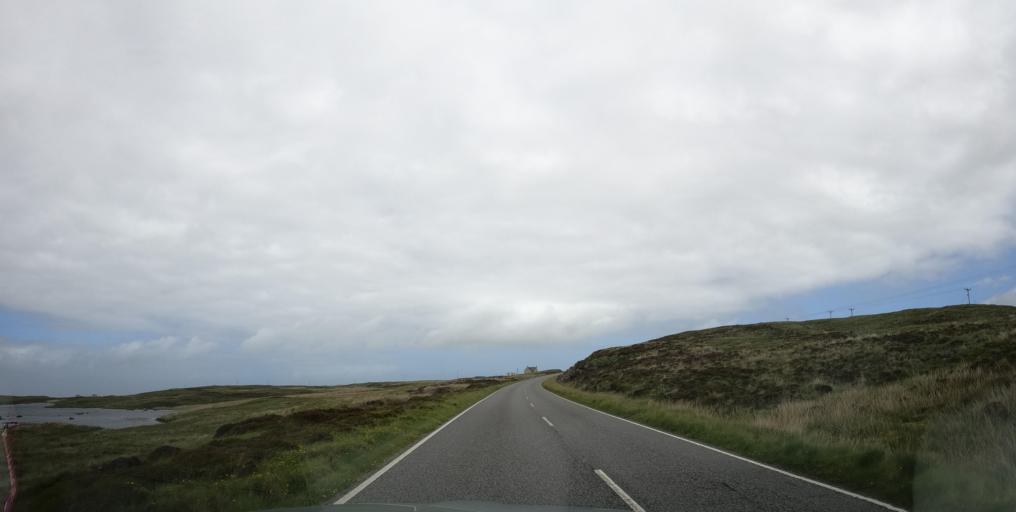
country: GB
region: Scotland
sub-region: Eilean Siar
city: Isle of South Uist
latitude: 57.2664
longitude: -7.3689
